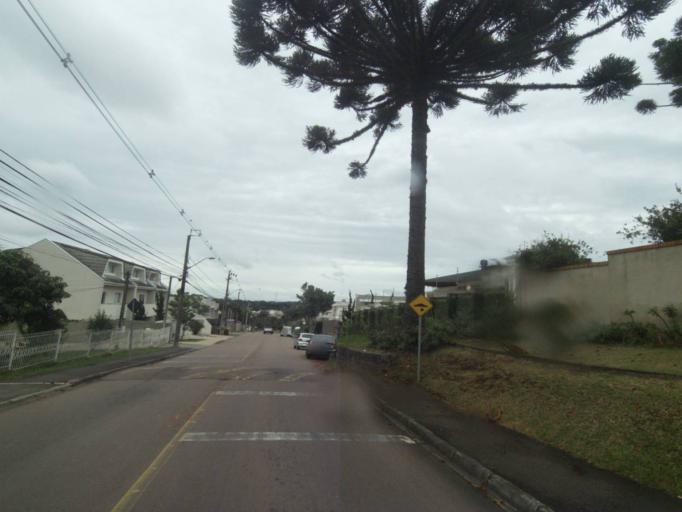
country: BR
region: Parana
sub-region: Curitiba
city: Curitiba
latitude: -25.4578
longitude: -49.3359
